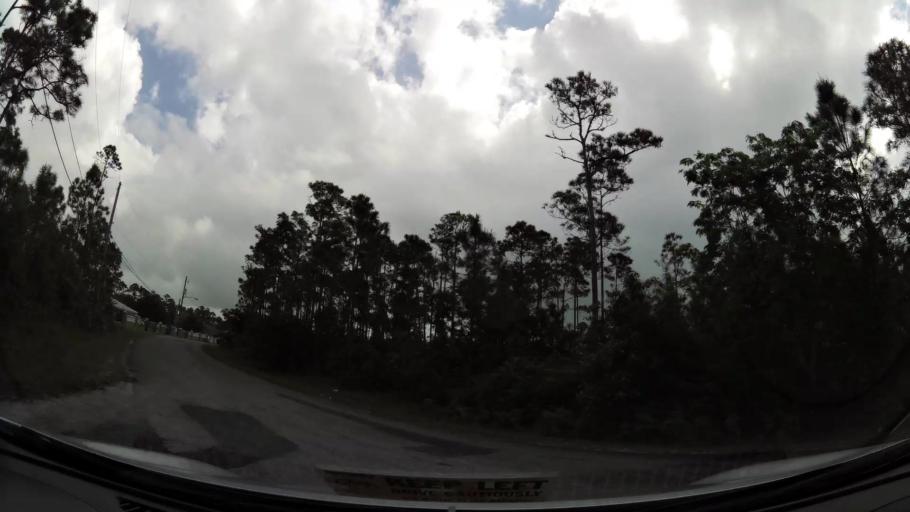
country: BS
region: Freeport
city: Lucaya
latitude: 26.5452
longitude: -78.5900
